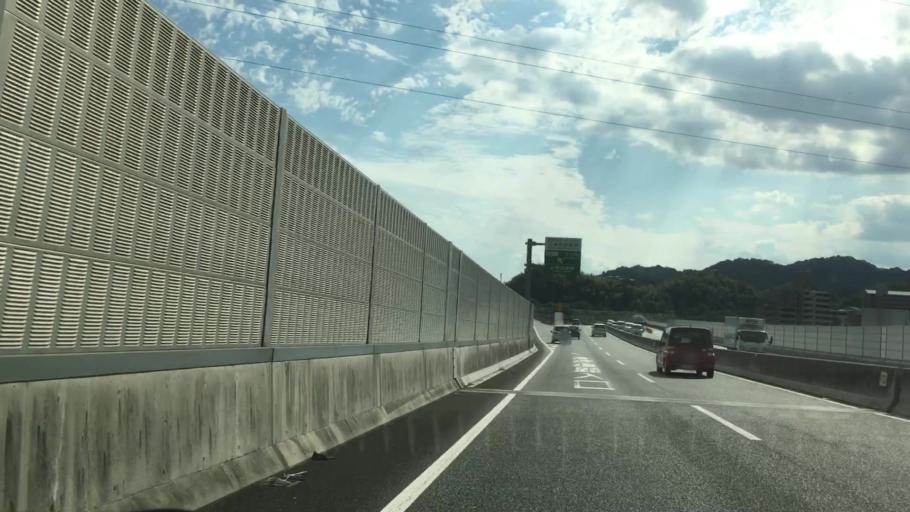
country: JP
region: Hiroshima
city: Hatsukaichi
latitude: 34.3506
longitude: 132.3199
